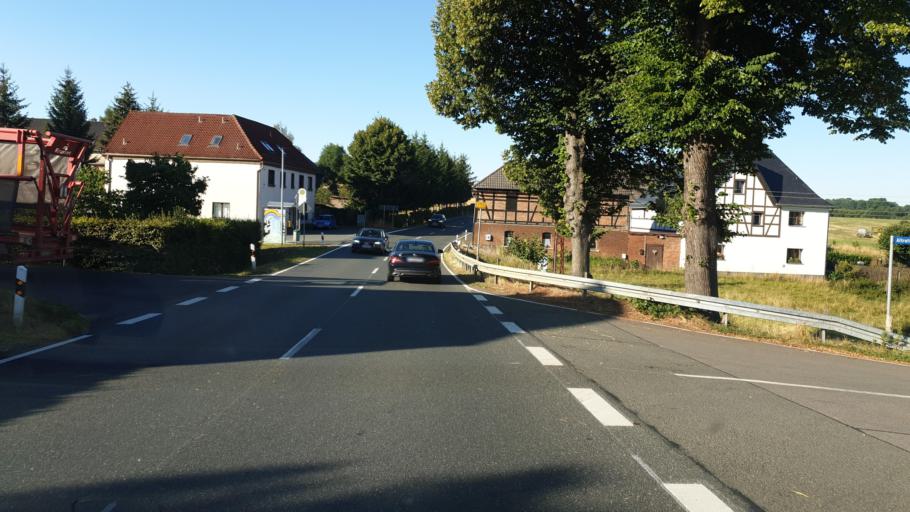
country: DE
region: Saxony
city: Neumark
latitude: 50.6694
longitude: 12.3862
